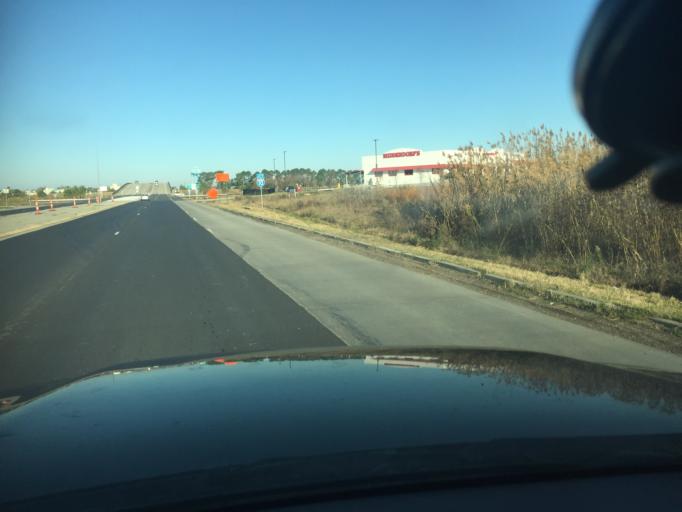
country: US
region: Louisiana
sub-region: Saint Tammany Parish
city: Eden Isle
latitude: 30.2191
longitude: -89.7794
